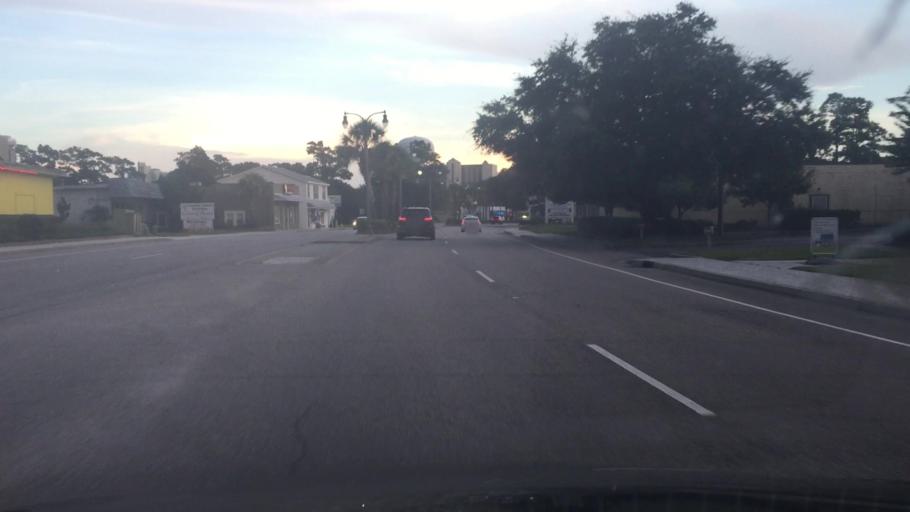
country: US
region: South Carolina
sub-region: Horry County
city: North Myrtle Beach
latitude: 33.8248
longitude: -78.6760
